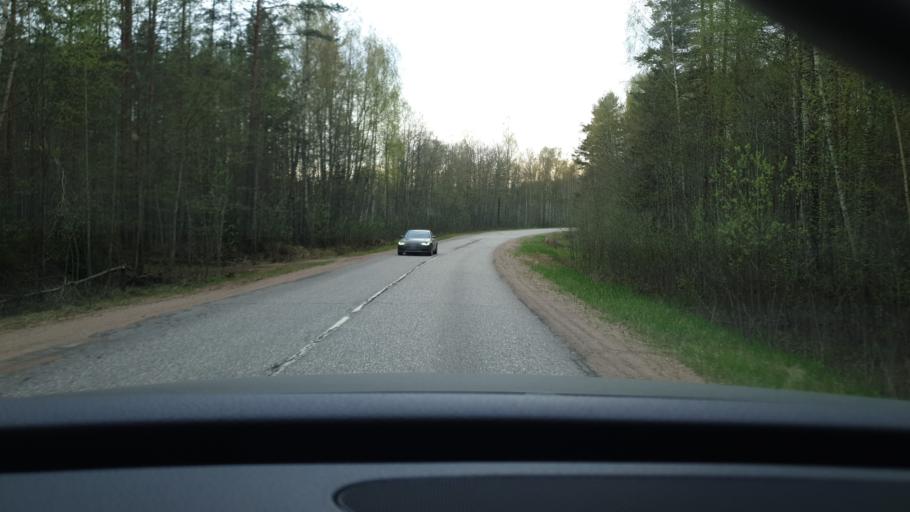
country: RU
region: Tverskaya
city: Bologoye
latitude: 57.9800
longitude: 34.0395
